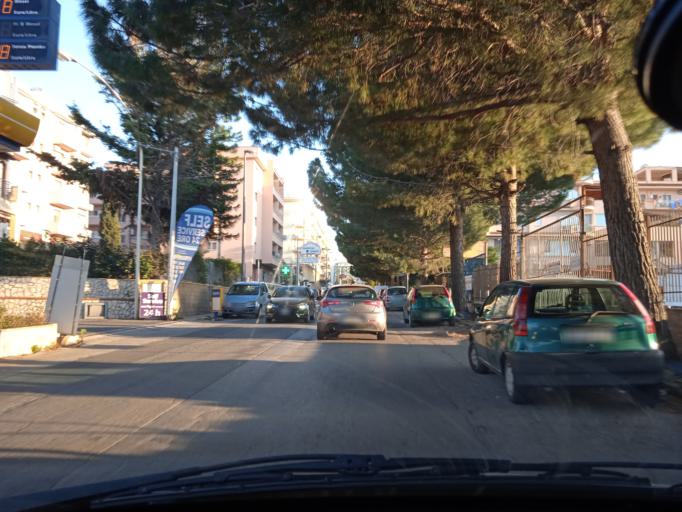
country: IT
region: Sicily
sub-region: Palermo
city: Bagheria
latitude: 38.0851
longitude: 13.5012
